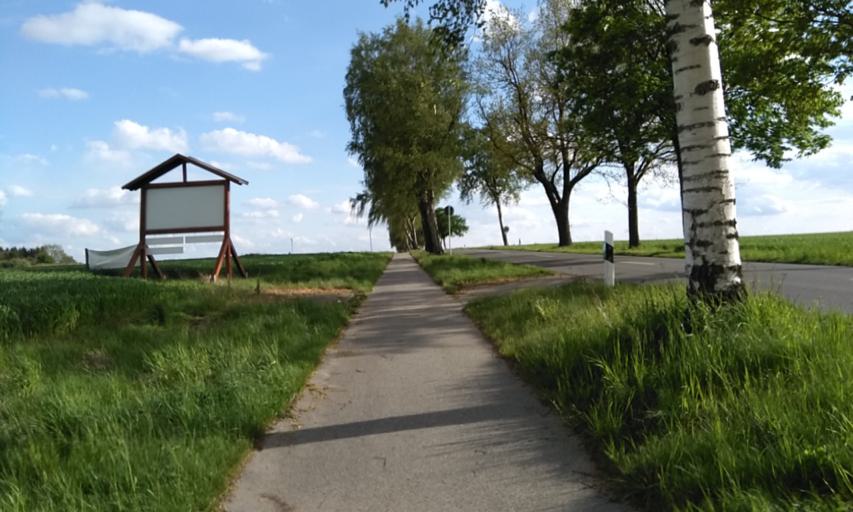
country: DE
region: Lower Saxony
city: Apensen
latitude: 53.4271
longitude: 9.6557
